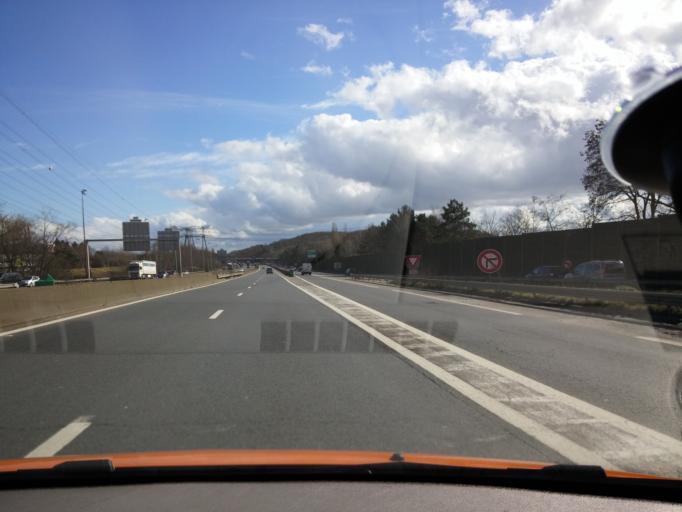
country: FR
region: Ile-de-France
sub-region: Departement de l'Essonne
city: Palaiseau
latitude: 48.7188
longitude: 2.2588
